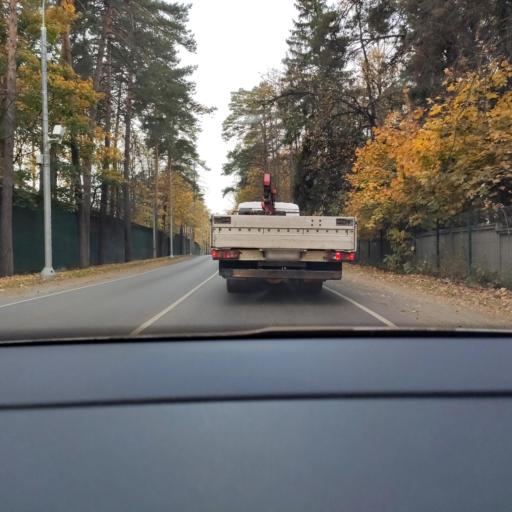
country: RU
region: Moskovskaya
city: Cherkizovo
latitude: 55.9706
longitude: 37.7752
